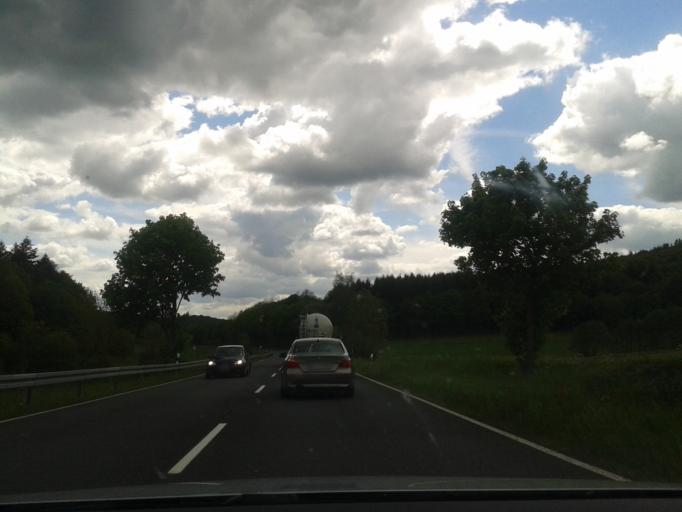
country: DE
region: Hesse
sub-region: Regierungsbezirk Giessen
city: Bad Endbach
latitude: 50.7185
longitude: 8.5047
